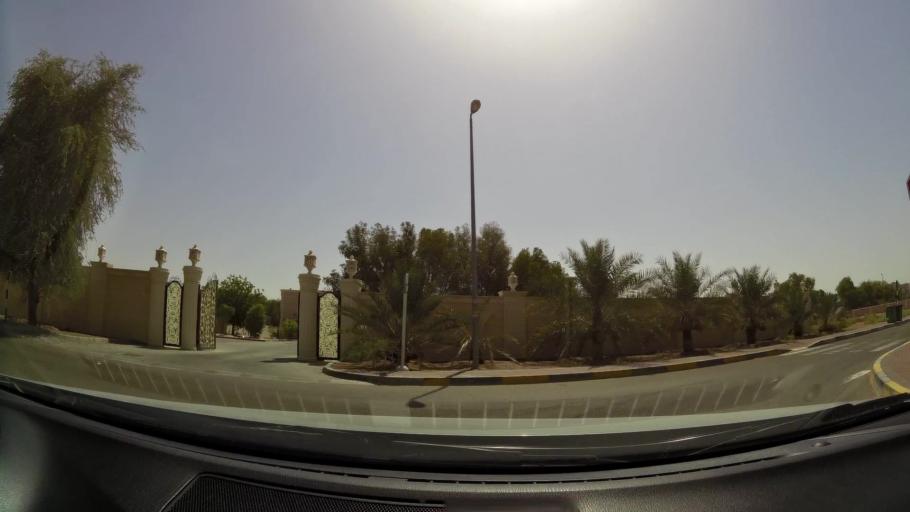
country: OM
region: Al Buraimi
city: Al Buraymi
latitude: 24.2982
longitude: 55.7527
